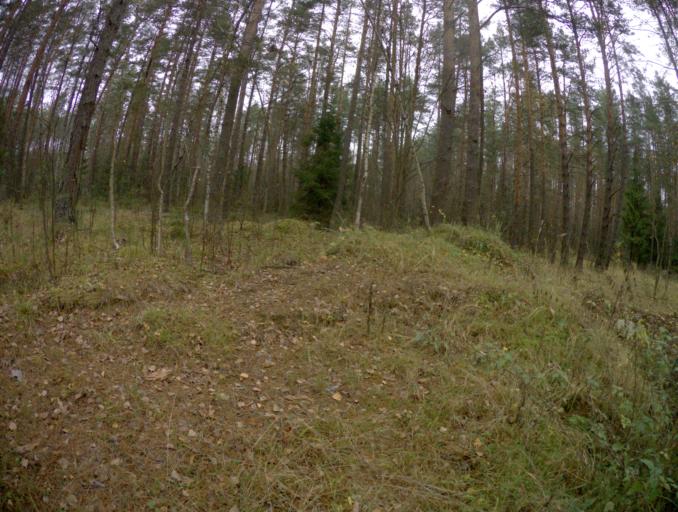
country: RU
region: Vladimir
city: Krasnyy Oktyabr'
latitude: 56.0097
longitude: 38.8368
